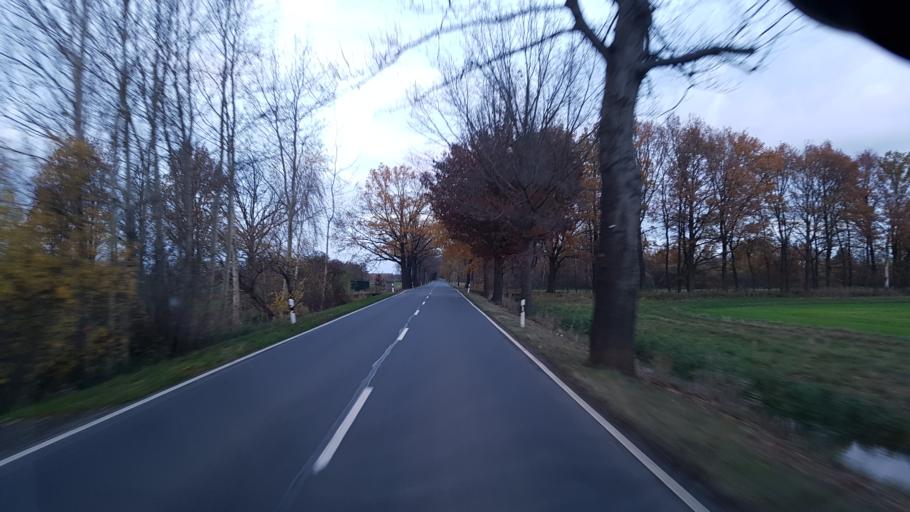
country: DE
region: Brandenburg
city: Schraden
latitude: 51.4530
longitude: 13.7113
